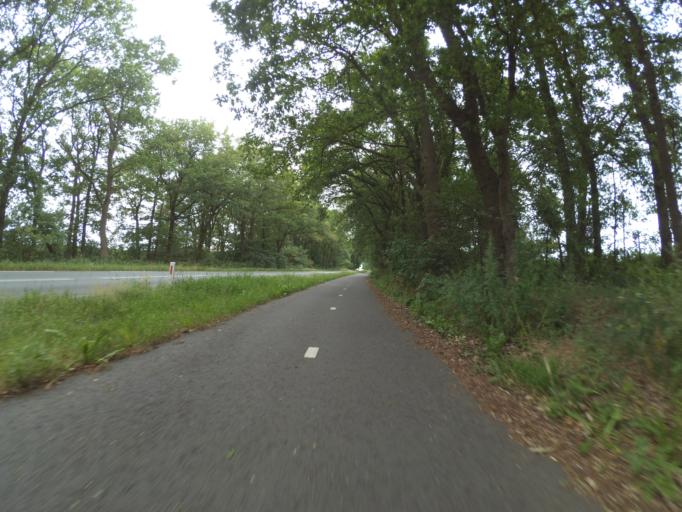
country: NL
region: Gelderland
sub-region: Gemeente Renkum
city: Wolfheze
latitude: 52.0459
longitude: 5.8076
